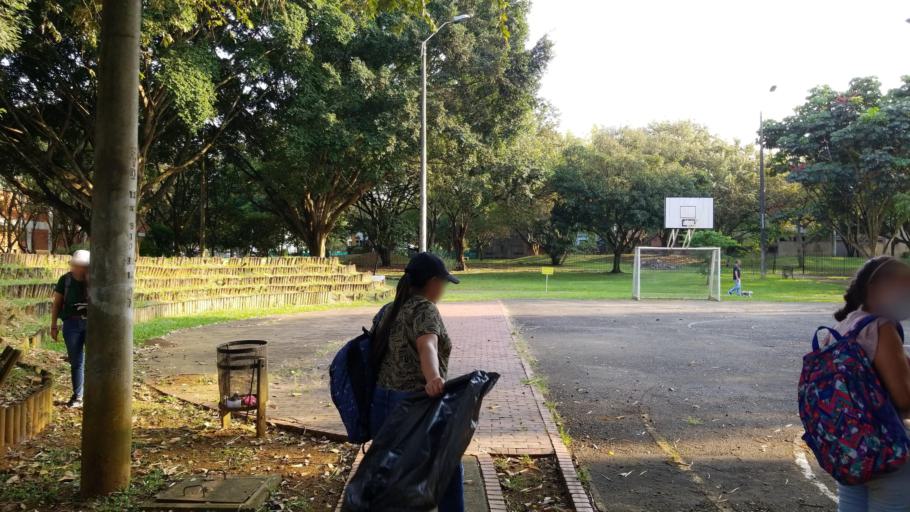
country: CO
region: Valle del Cauca
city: Cali
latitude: 3.3855
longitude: -76.5407
